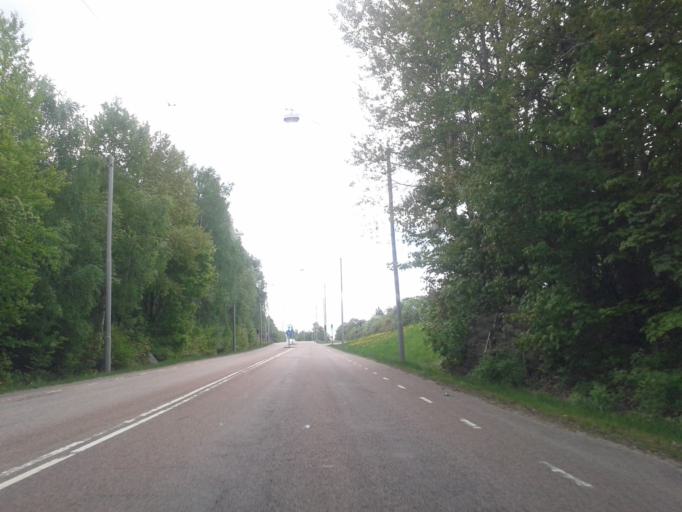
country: SE
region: Vaestra Goetaland
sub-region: Goteborg
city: Gardsten
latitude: 57.8077
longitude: 12.0336
